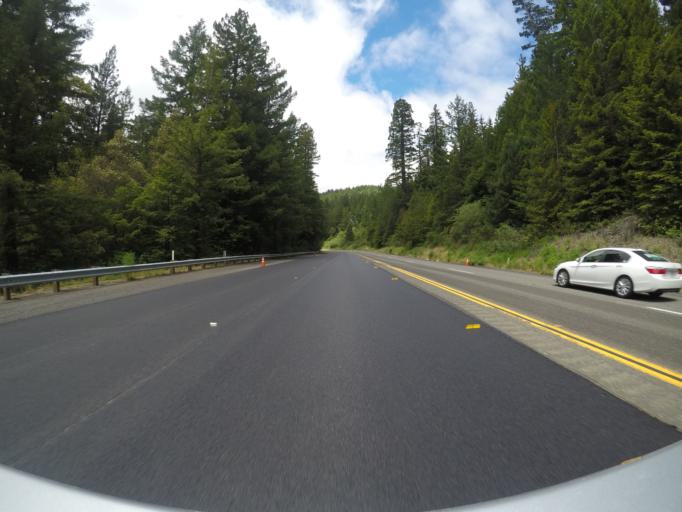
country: US
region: California
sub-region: Humboldt County
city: Redway
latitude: 40.3008
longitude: -123.8924
